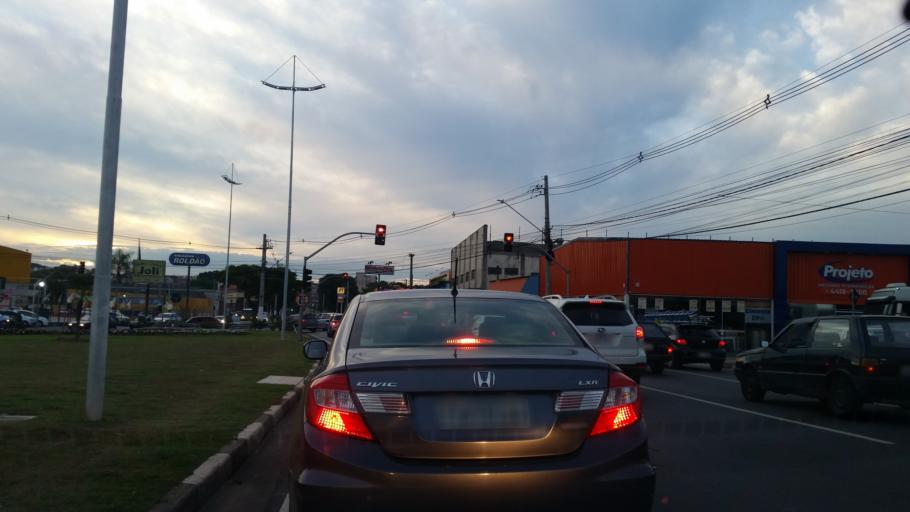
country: BR
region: Sao Paulo
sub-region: Atibaia
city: Atibaia
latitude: -23.1162
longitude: -46.5745
